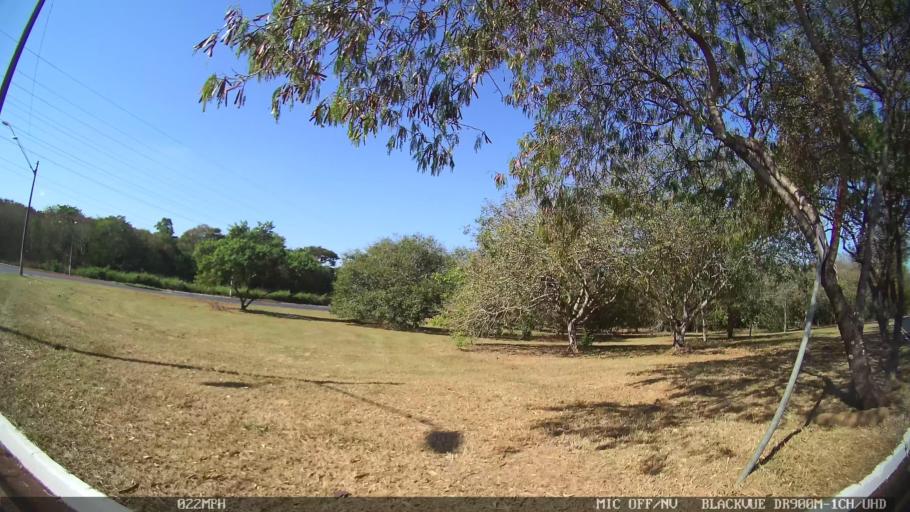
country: BR
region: Sao Paulo
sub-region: Ribeirao Preto
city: Ribeirao Preto
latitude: -21.2231
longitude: -47.7692
